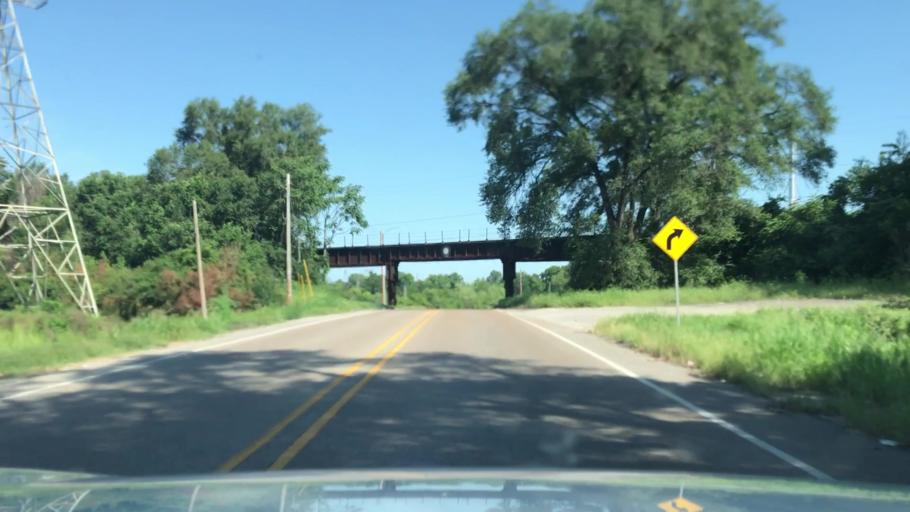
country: US
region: Illinois
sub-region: Madison County
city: Venice
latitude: 38.6620
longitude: -90.1690
